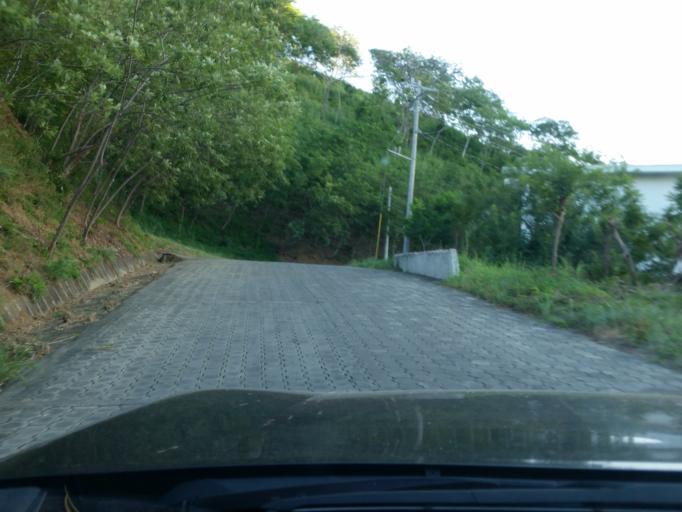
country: NI
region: Rivas
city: San Juan del Sur
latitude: 11.2484
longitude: -85.8679
